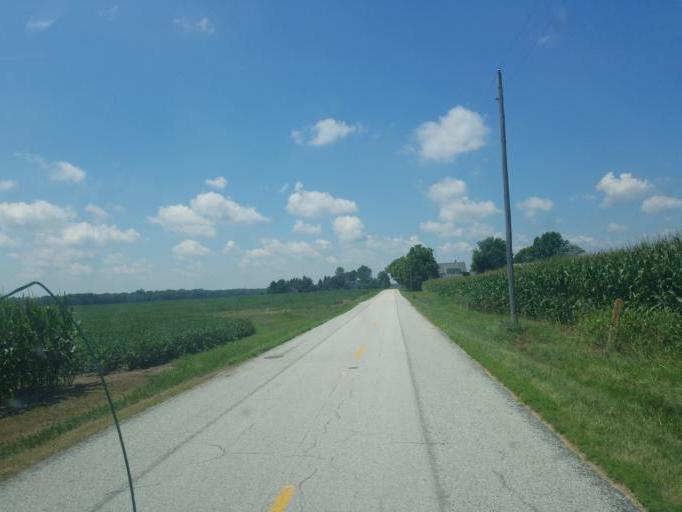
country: US
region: Ohio
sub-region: Allen County
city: Spencerville
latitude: 40.6666
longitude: -84.4254
